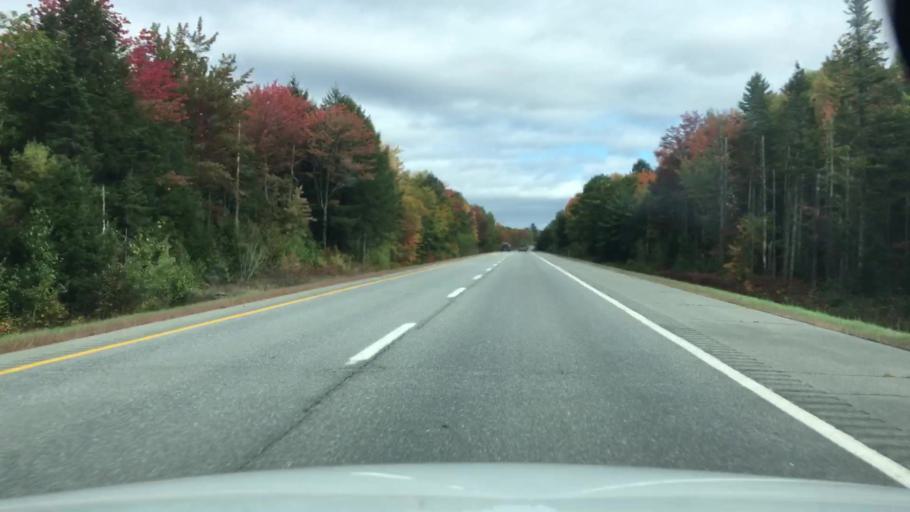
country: US
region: Maine
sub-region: Penobscot County
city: Carmel
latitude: 44.7735
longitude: -69.0245
